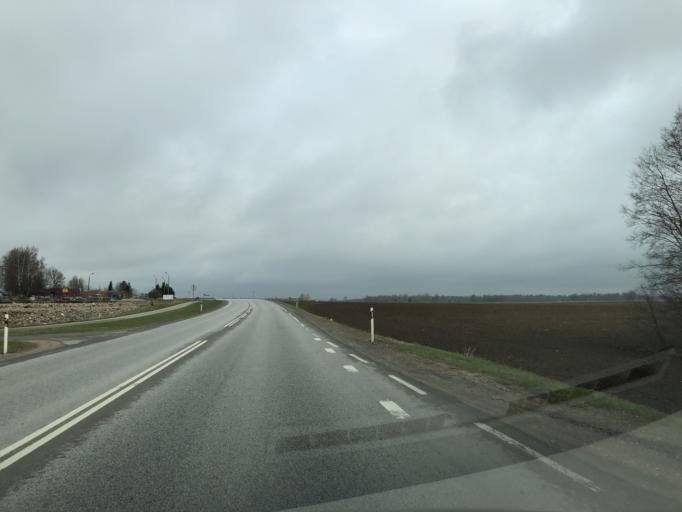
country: EE
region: Jogevamaa
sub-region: Jogeva linn
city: Jogeva
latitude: 58.7462
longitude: 26.3610
